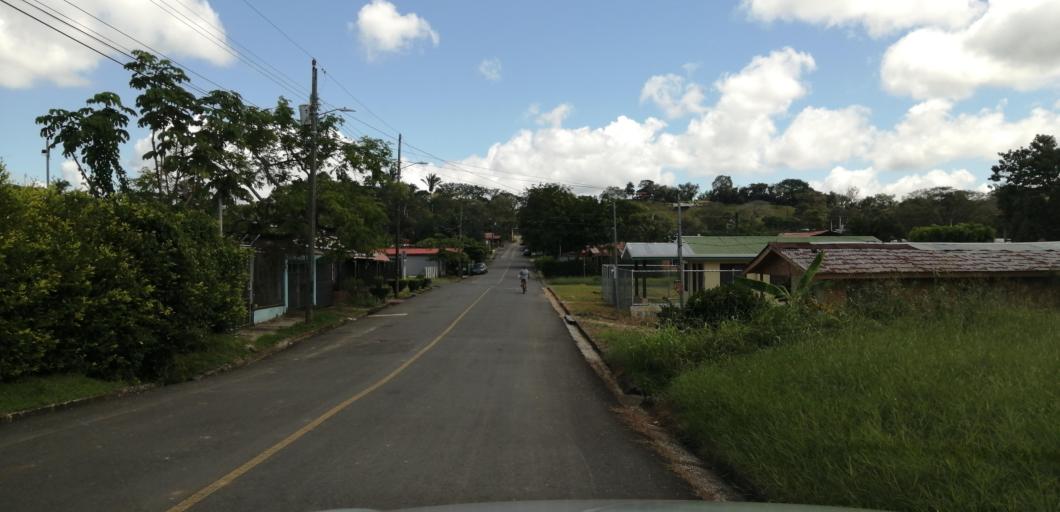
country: CR
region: Guanacaste
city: Hojancha
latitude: 10.0567
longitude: -85.4175
